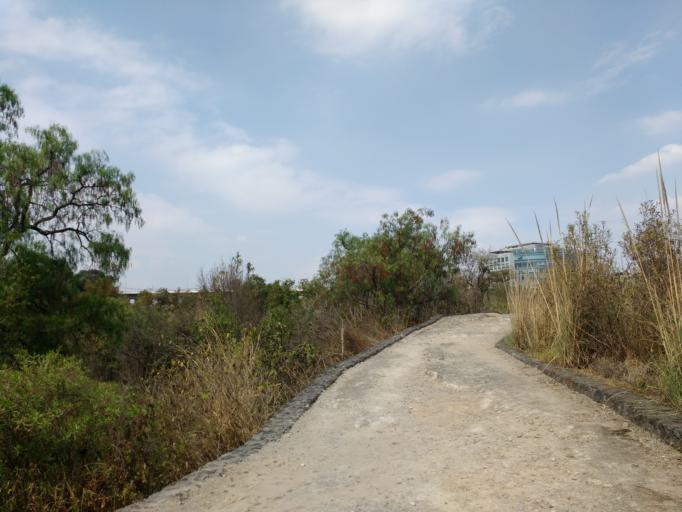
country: MX
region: Mexico City
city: Tlalpan
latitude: 19.3002
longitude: -99.1844
